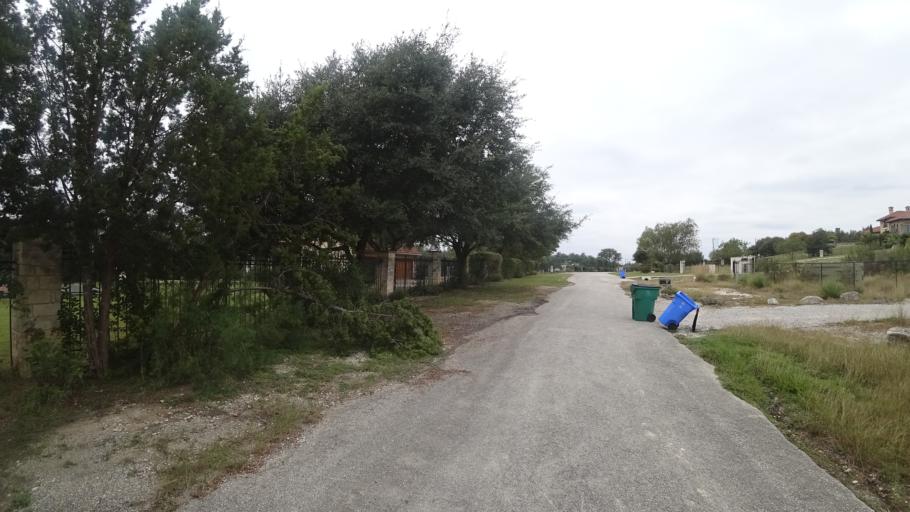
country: US
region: Texas
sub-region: Travis County
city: Lakeway
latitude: 30.3696
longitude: -97.9403
